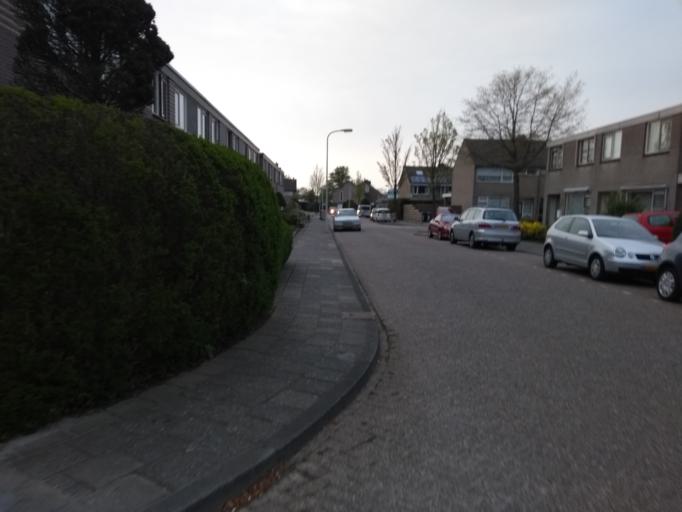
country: NL
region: Friesland
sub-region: Gemeente Smallingerland
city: Drachten
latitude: 53.1032
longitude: 6.1182
